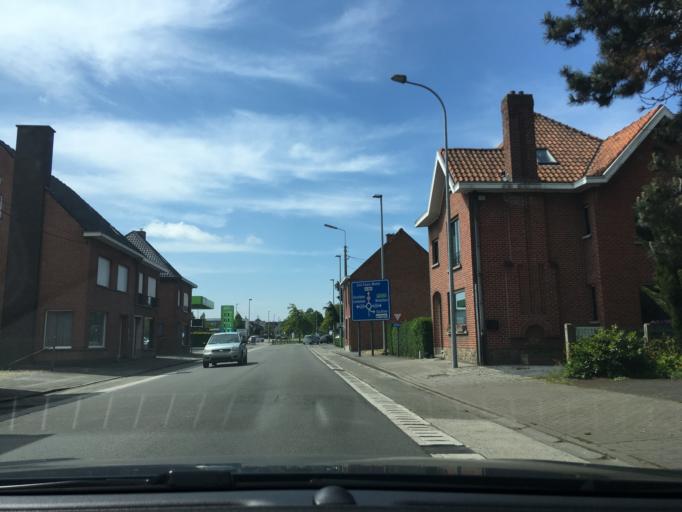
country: BE
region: Flanders
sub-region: Provincie West-Vlaanderen
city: Izegem
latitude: 50.9160
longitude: 3.1979
